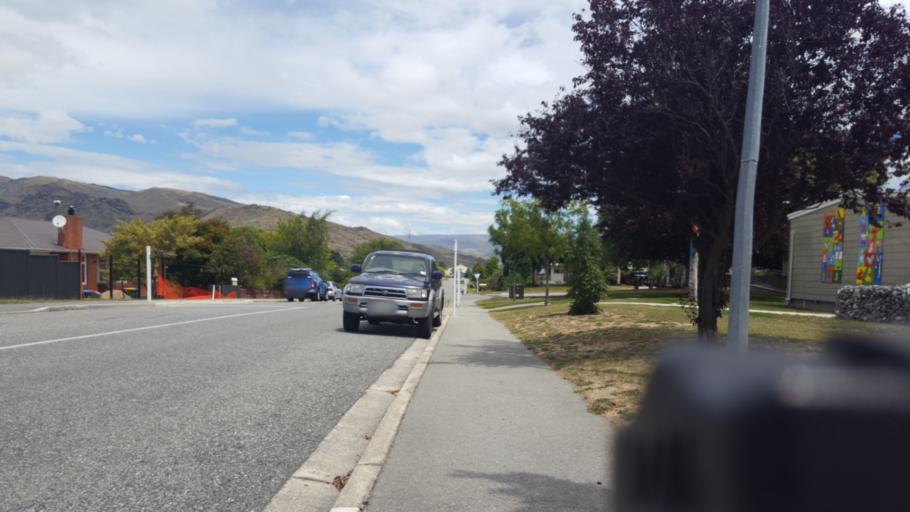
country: NZ
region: Otago
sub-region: Queenstown-Lakes District
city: Wanaka
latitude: -45.0449
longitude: 169.2046
